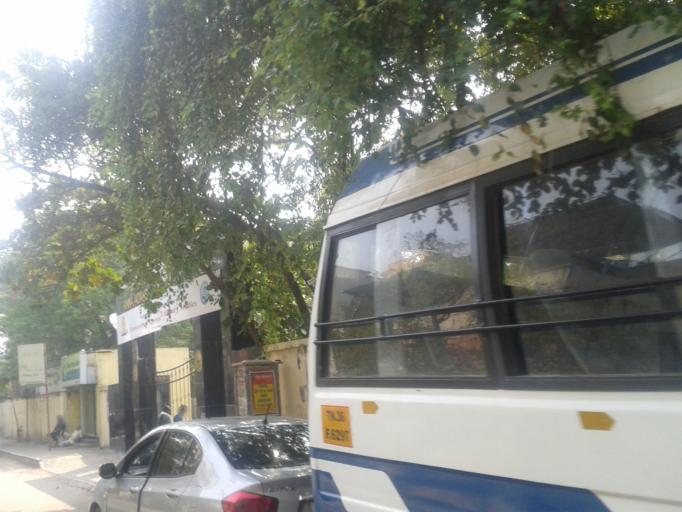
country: IN
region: Tamil Nadu
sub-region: Chennai
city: Chetput
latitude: 13.0806
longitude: 80.2106
